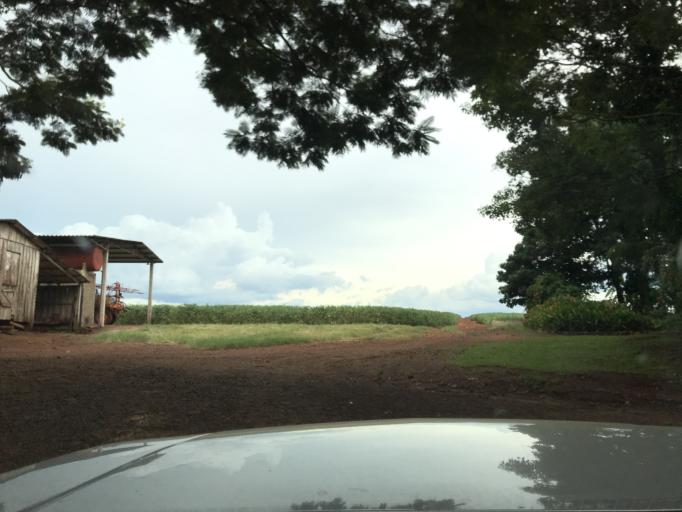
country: BR
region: Parana
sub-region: Palotina
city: Palotina
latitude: -24.2723
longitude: -53.7861
